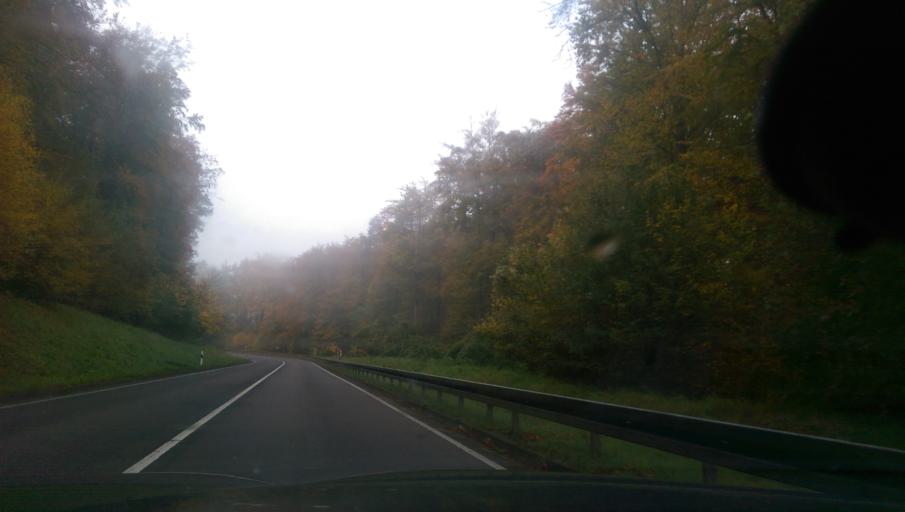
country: DE
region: Bavaria
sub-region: Regierungsbezirk Unterfranken
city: Oerlenbach
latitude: 50.1542
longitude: 10.1045
